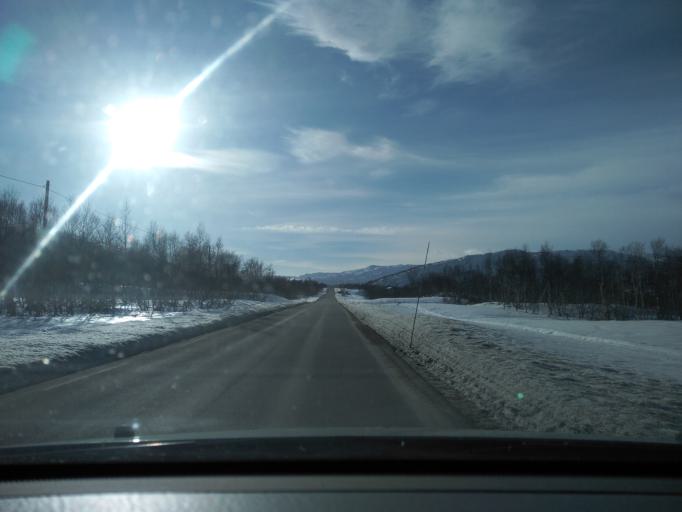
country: NO
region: Aust-Agder
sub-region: Bykle
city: Hovden
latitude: 59.6498
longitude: 7.4740
